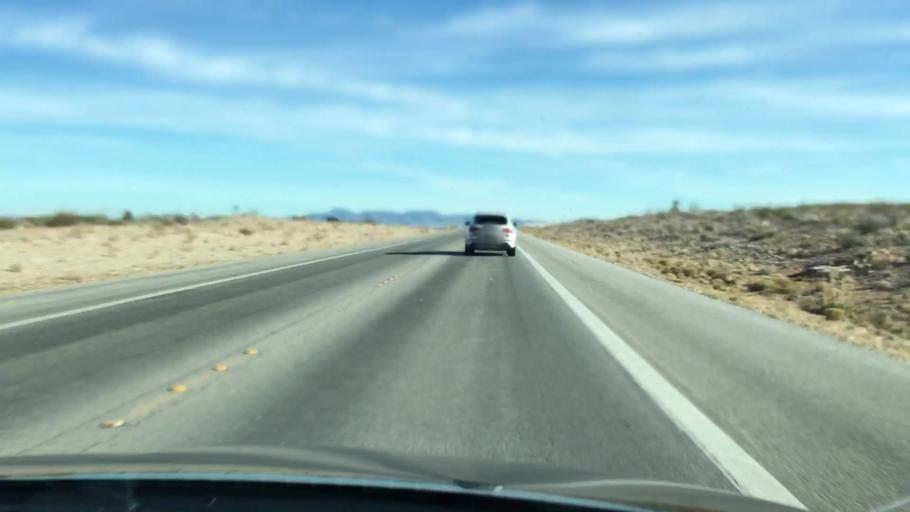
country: US
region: Nevada
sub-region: Clark County
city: Summerlin South
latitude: 36.0414
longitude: -115.3734
